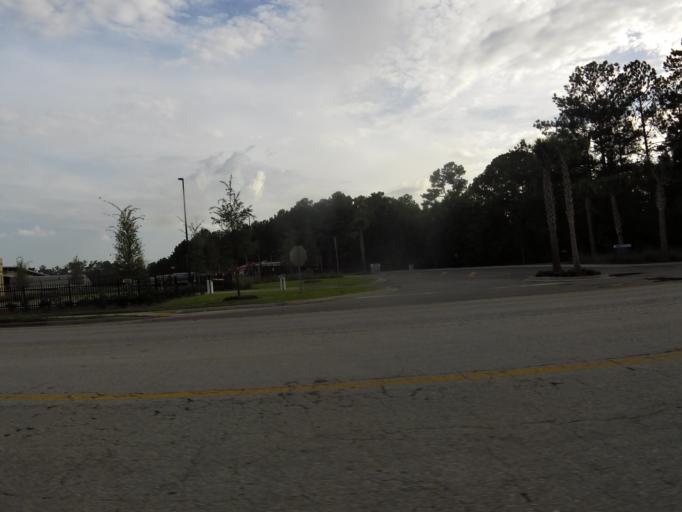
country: US
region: Florida
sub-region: Duval County
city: Jacksonville
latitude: 30.3372
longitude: -81.7678
